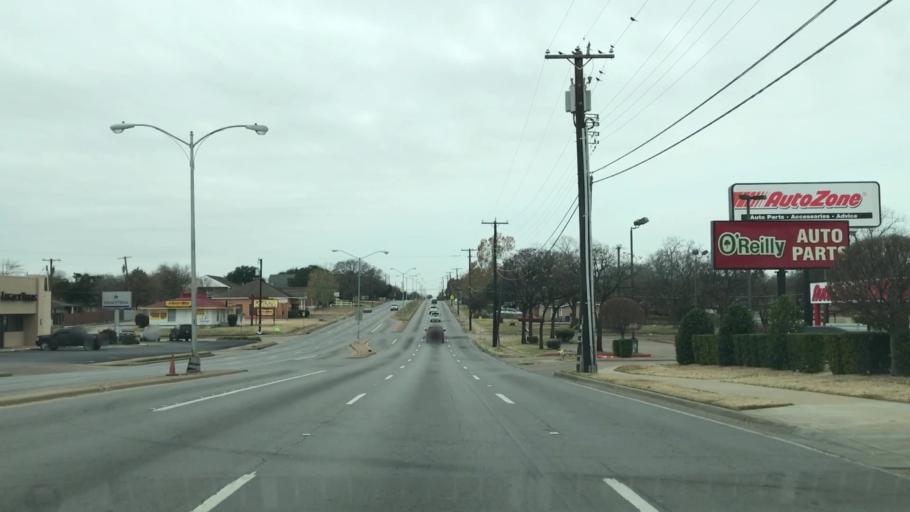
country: US
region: Texas
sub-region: Dallas County
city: Cockrell Hill
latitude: 32.7204
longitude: -96.8581
